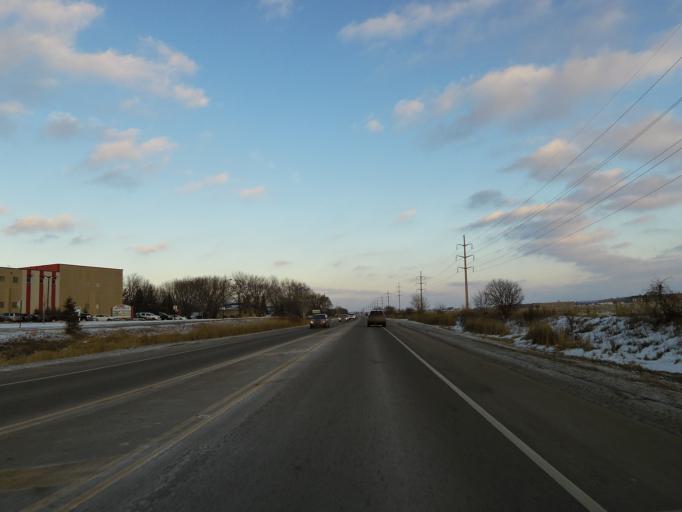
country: US
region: Minnesota
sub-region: Dakota County
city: Lakeville
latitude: 44.6380
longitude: -93.2661
